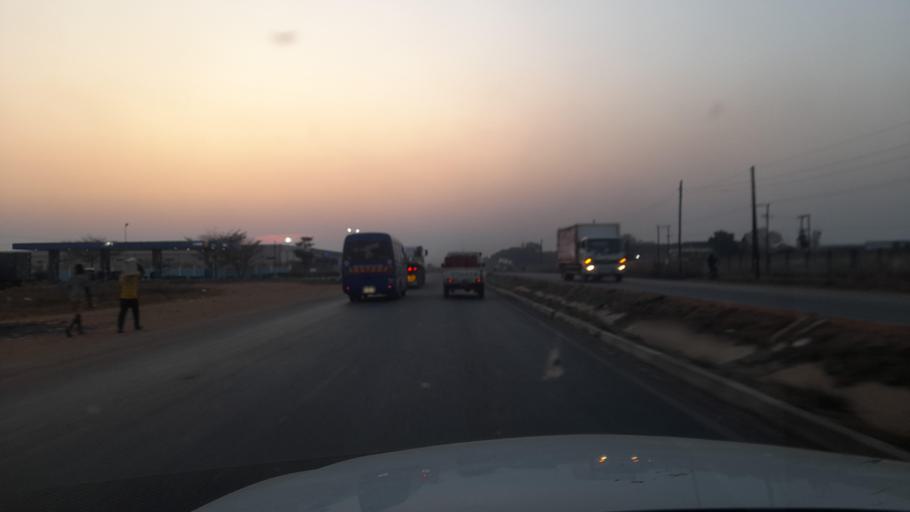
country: ZM
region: Copperbelt
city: Kitwe
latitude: -12.7711
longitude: 28.1838
